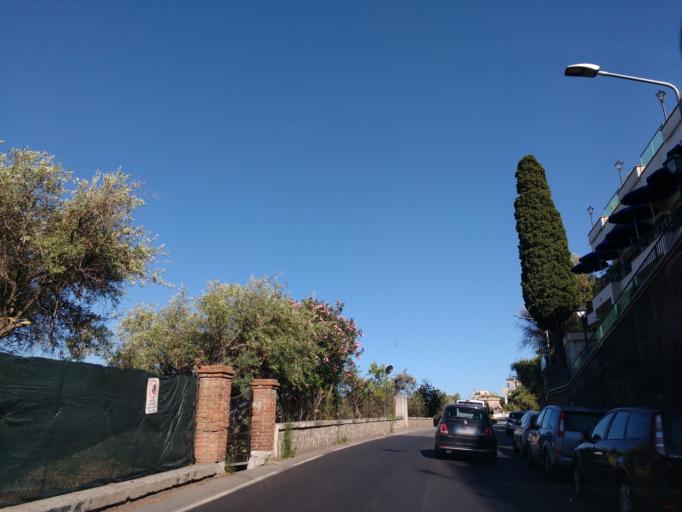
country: IT
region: Sicily
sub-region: Messina
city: Taormina
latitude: 37.8588
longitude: 15.2970
